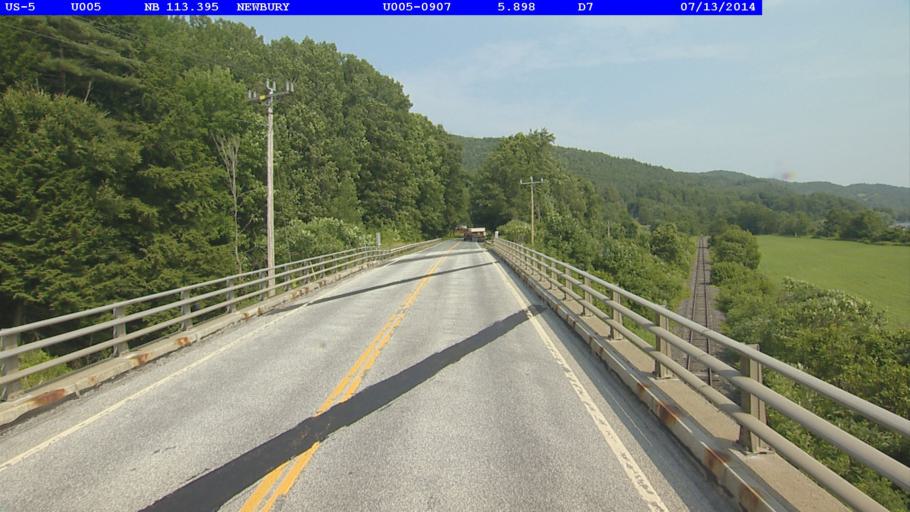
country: US
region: New Hampshire
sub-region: Grafton County
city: North Haverhill
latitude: 44.1055
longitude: -72.0551
